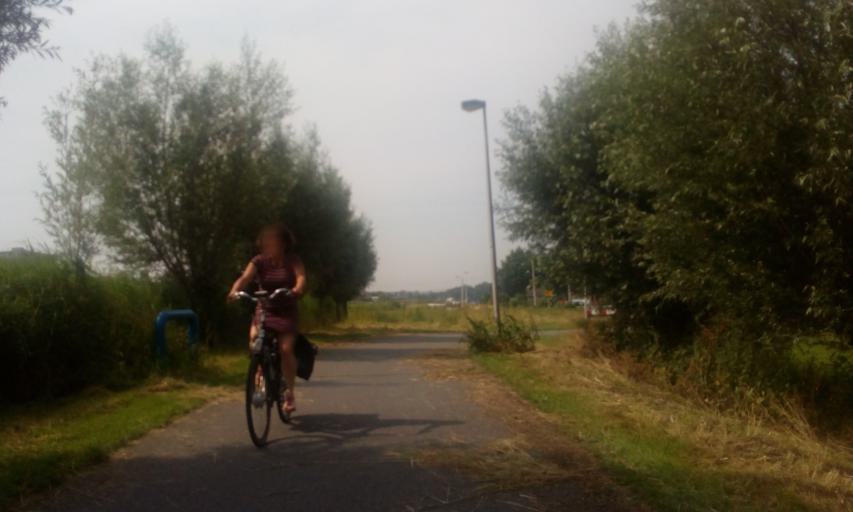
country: NL
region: South Holland
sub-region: Gemeente Krimpen aan den IJssel
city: Krimpen aan den IJssel
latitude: 51.9571
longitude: 4.6130
